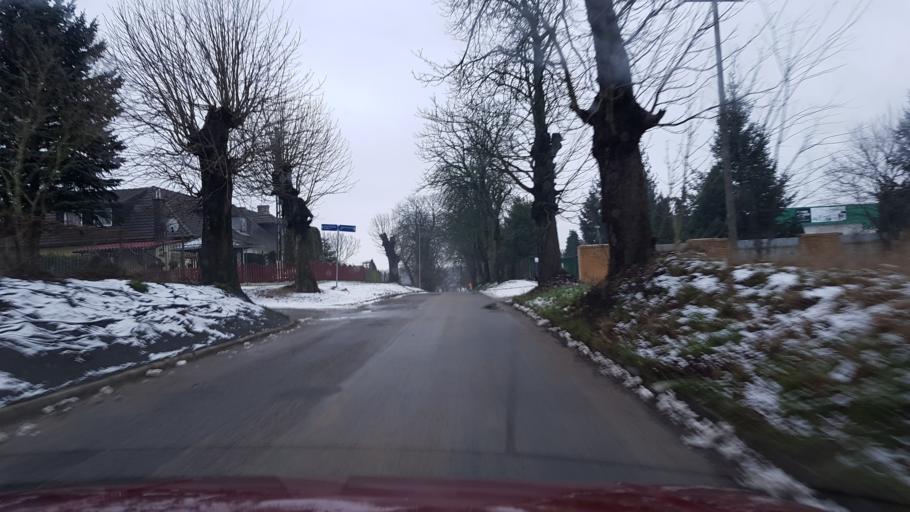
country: PL
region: West Pomeranian Voivodeship
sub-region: Powiat goleniowski
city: Mosty
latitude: 53.5219
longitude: 14.9439
